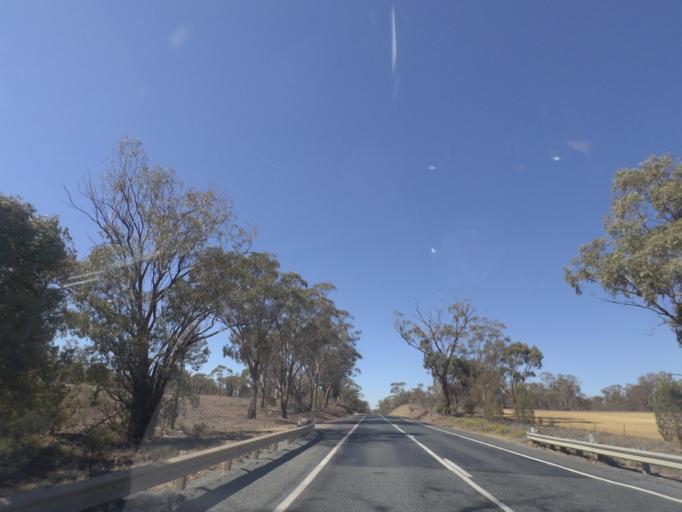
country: AU
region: New South Wales
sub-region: Bland
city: West Wyalong
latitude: -34.1657
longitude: 147.1160
